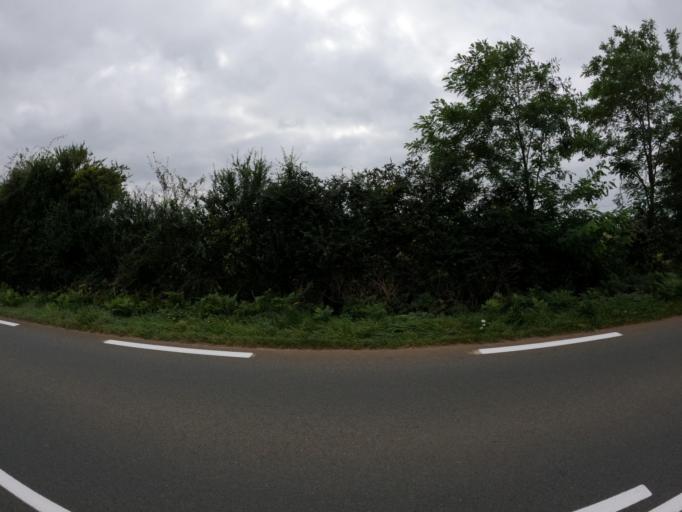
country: FR
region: Poitou-Charentes
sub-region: Departement de la Vienne
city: Availles-Limouzine
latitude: 46.1170
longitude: 0.5468
